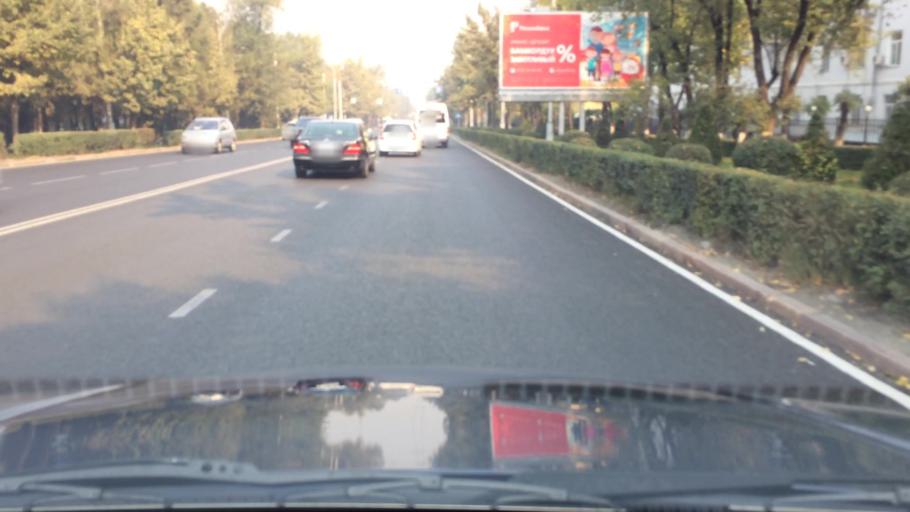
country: KG
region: Chuy
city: Bishkek
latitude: 42.8454
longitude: 74.5862
